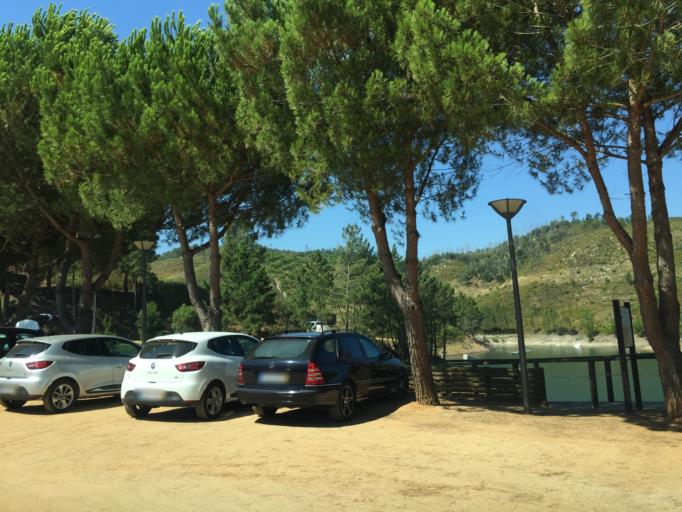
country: PT
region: Santarem
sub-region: Constancia
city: Constancia
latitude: 39.5452
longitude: -8.2772
